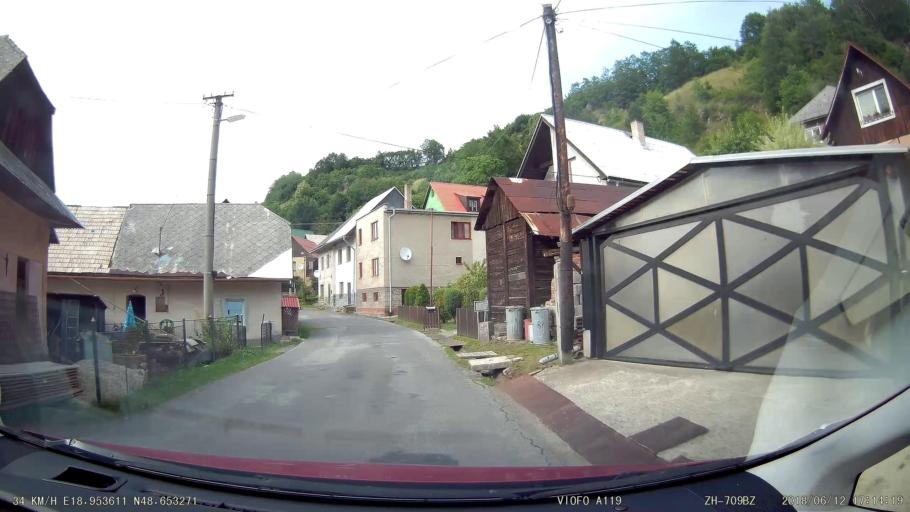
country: SK
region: Banskobystricky
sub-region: Okres Ziar nad Hronom
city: Kremnica
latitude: 48.6533
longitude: 18.9535
